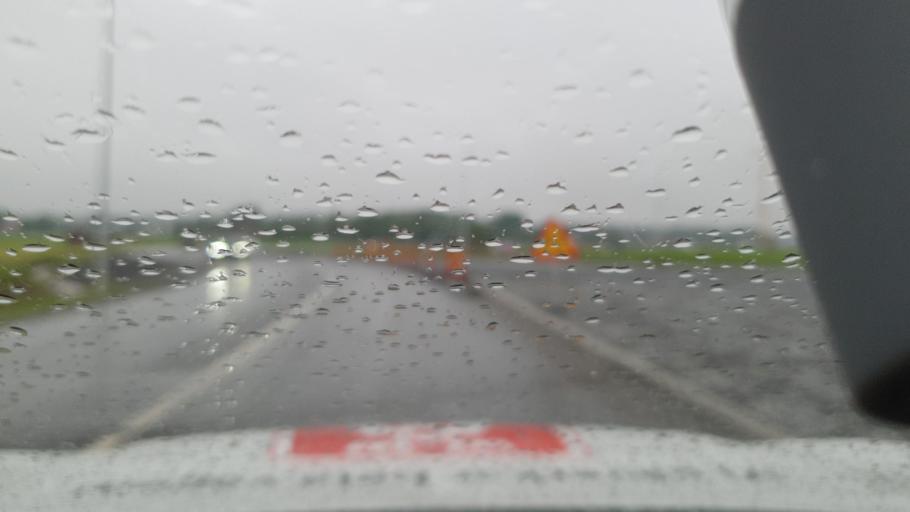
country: SE
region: Vaesterbotten
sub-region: Umea Kommun
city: Roback
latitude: 63.8118
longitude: 20.2118
